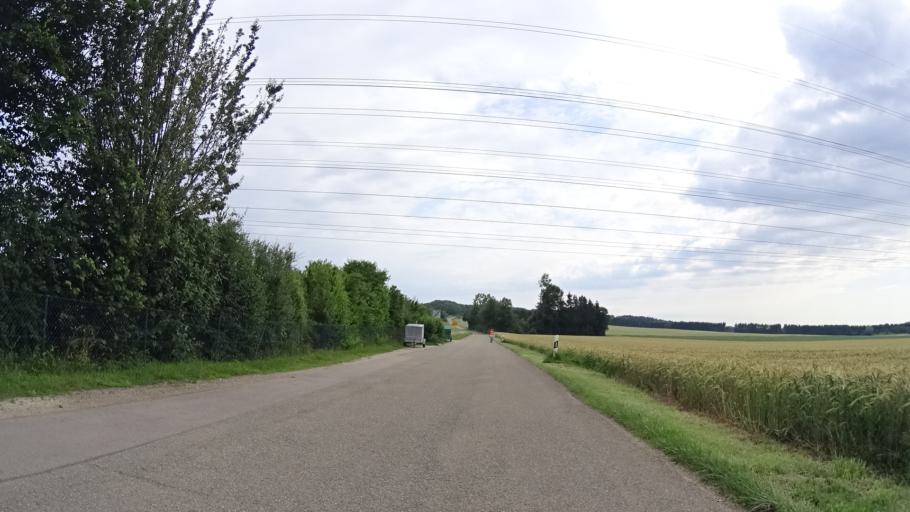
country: DE
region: Bavaria
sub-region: Upper Bavaria
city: Wettstetten
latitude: 48.8272
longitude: 11.4204
